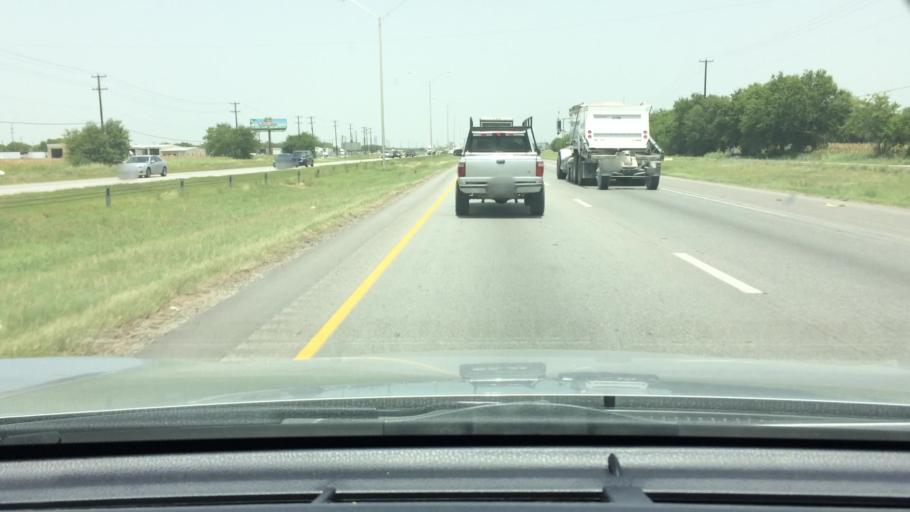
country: US
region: Texas
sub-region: Bexar County
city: Kirby
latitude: 29.4159
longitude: -98.3892
